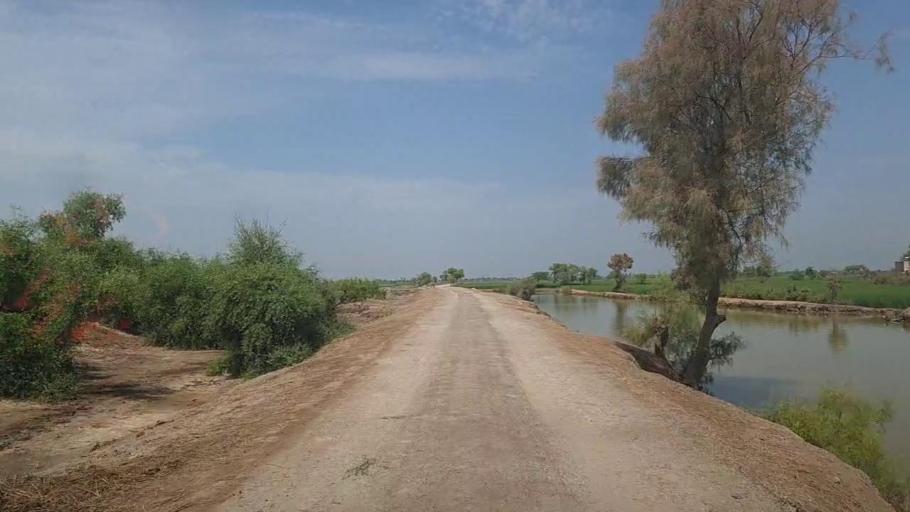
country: PK
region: Sindh
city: Thul
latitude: 28.2953
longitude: 68.6812
